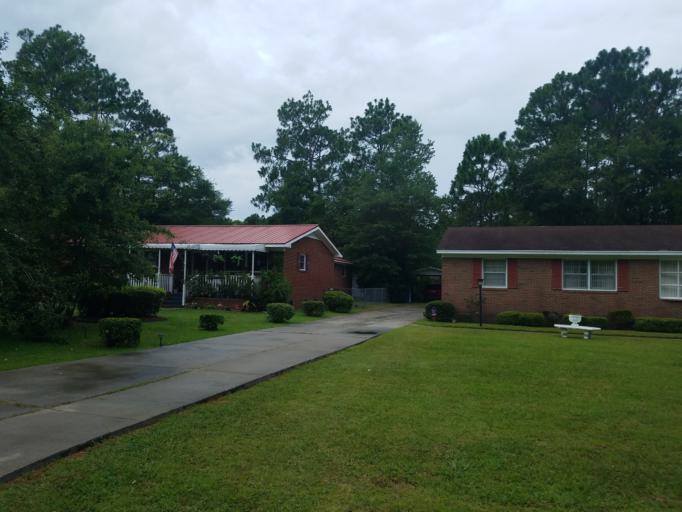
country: US
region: North Carolina
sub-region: New Hanover County
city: Kings Grant
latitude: 34.2395
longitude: -77.8600
